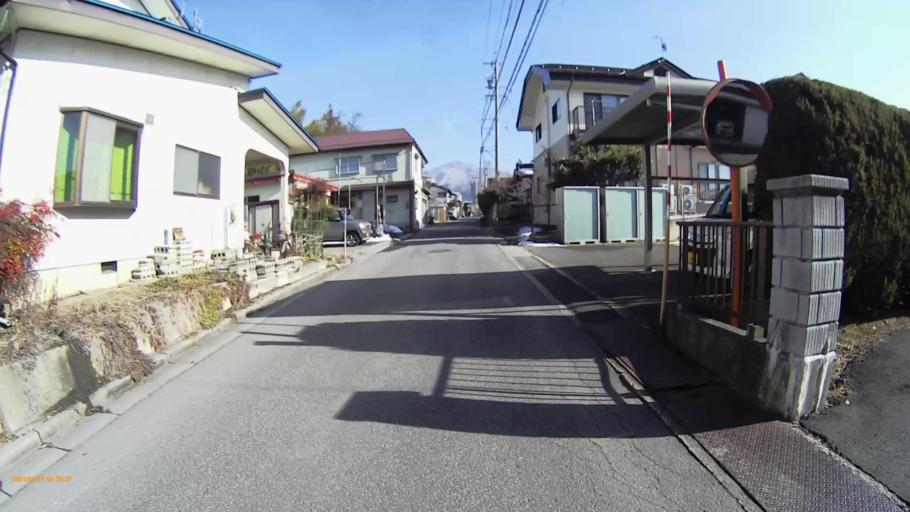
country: JP
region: Nagano
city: Nakano
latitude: 36.7430
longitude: 138.4095
